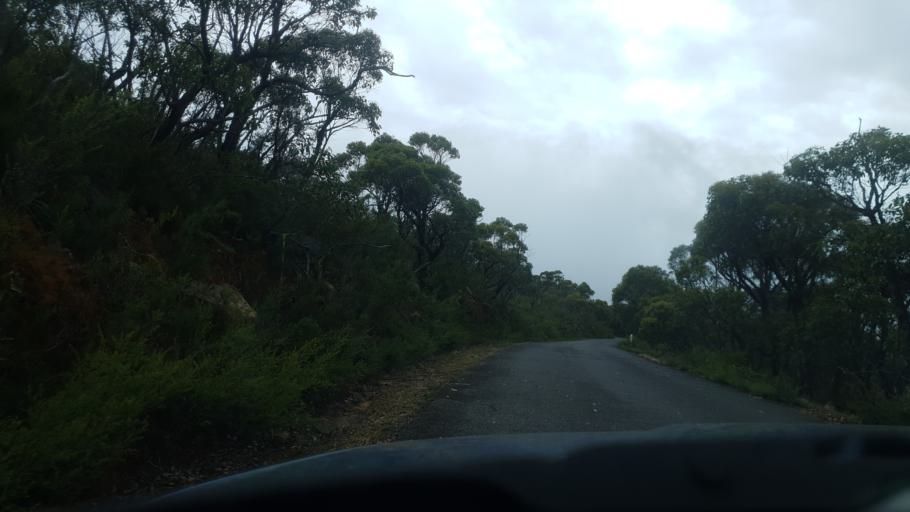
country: AU
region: Victoria
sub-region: Northern Grampians
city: Stawell
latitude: -37.2675
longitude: 142.5773
